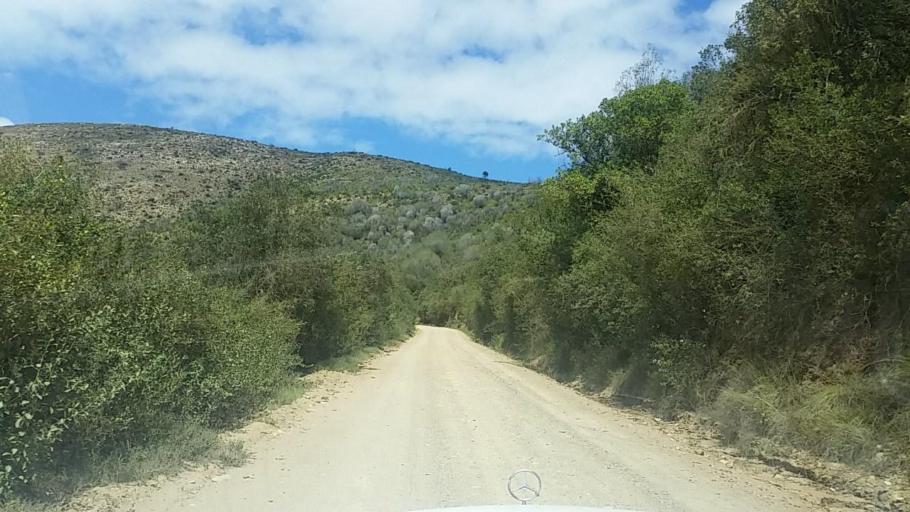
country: ZA
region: Western Cape
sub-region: Eden District Municipality
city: Knysna
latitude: -33.8158
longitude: 23.1746
